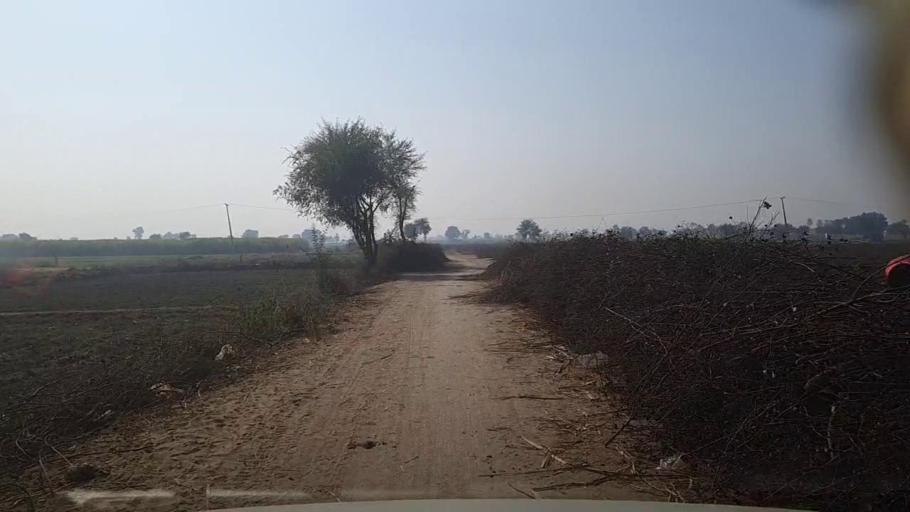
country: PK
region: Sindh
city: Kandiari
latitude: 26.9963
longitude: 68.4910
